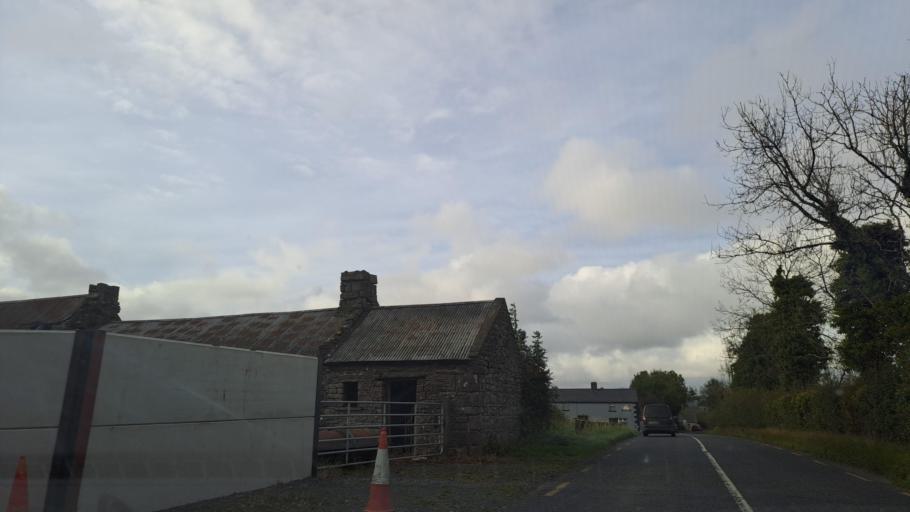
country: IE
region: Ulster
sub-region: An Cabhan
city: Kingscourt
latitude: 53.8470
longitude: -6.7762
